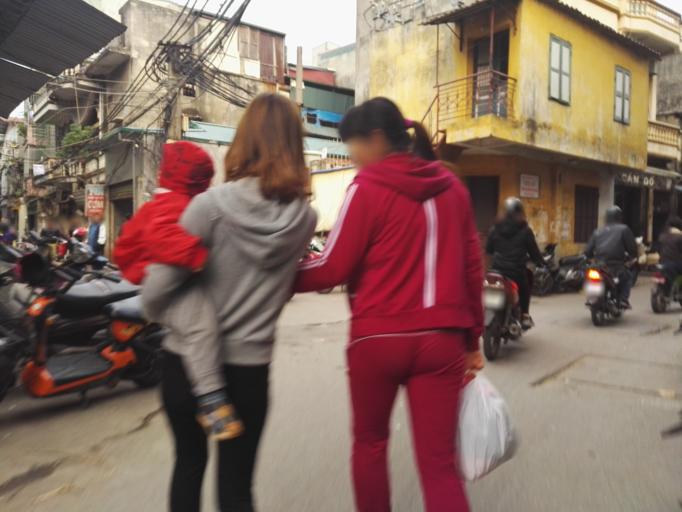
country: VN
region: Ha Noi
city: Hoan Kiem
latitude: 21.0429
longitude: 105.8509
